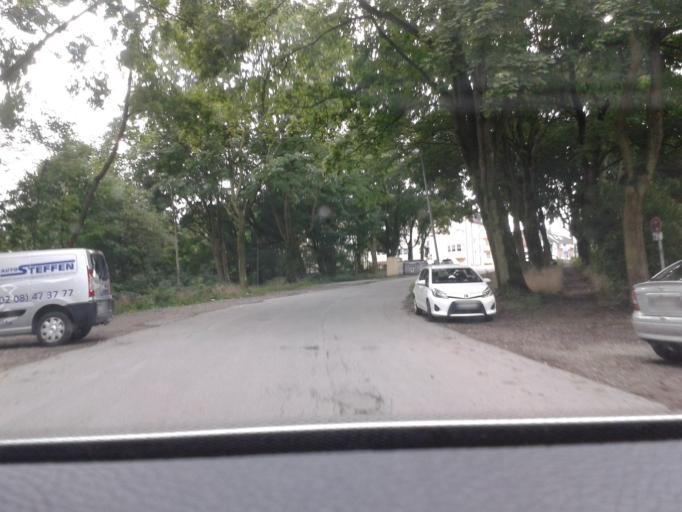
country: DE
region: North Rhine-Westphalia
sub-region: Regierungsbezirk Dusseldorf
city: Muelheim (Ruhr)
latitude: 51.4332
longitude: 6.8298
